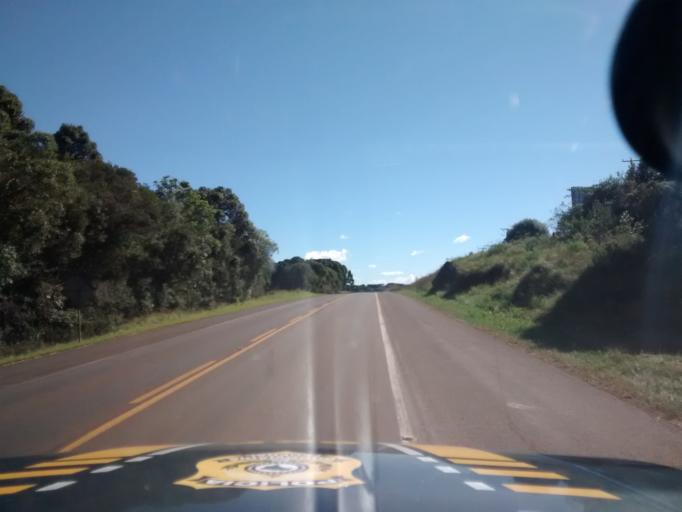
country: BR
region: Rio Grande do Sul
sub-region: Vacaria
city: Vacaria
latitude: -28.3558
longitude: -51.1102
